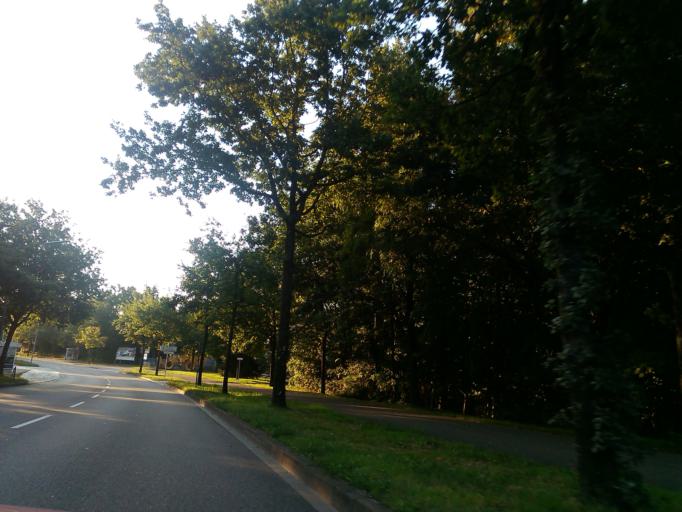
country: DE
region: Baden-Wuerttemberg
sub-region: Karlsruhe Region
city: Karlsruhe
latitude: 48.9968
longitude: 8.4316
